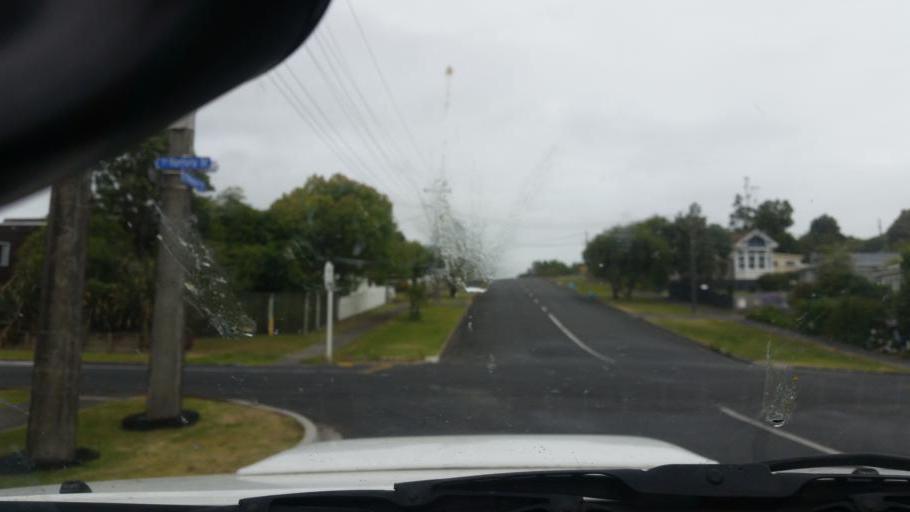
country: NZ
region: Northland
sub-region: Kaipara District
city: Dargaville
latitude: -35.9366
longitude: 173.8667
